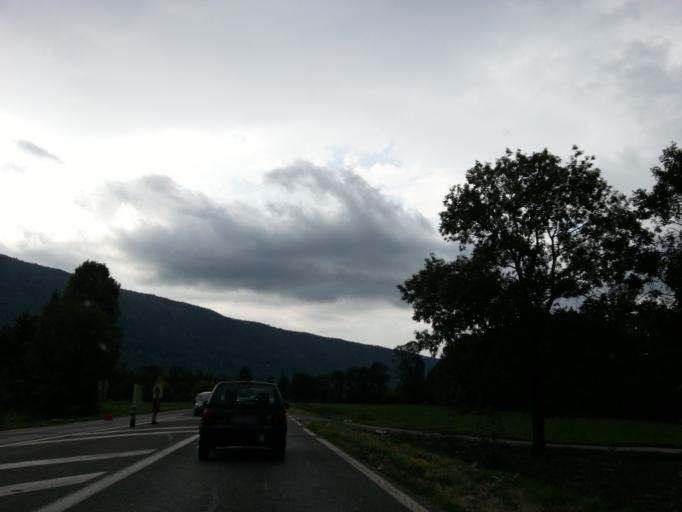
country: FR
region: Rhone-Alpes
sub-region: Departement de la Haute-Savoie
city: Saint-Jorioz
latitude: 45.8394
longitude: 6.1563
